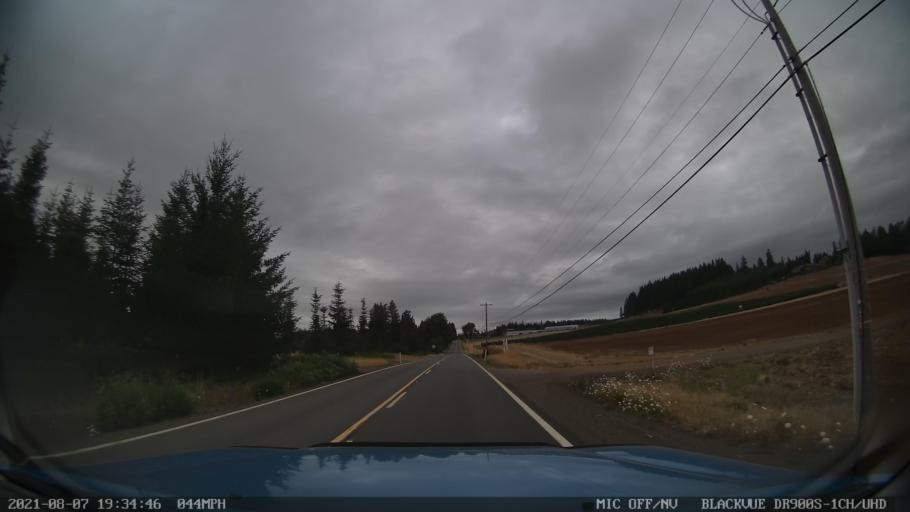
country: US
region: Oregon
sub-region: Marion County
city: Silverton
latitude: 44.9210
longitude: -122.6567
